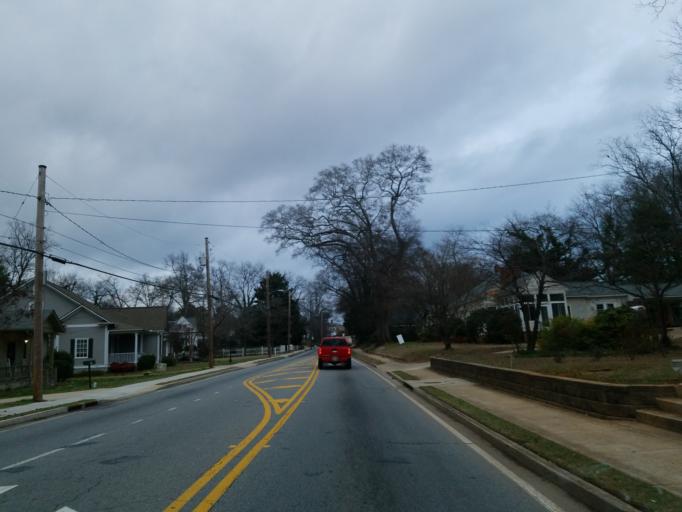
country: US
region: Georgia
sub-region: Bartow County
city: Cartersville
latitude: 34.1611
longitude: -84.8021
